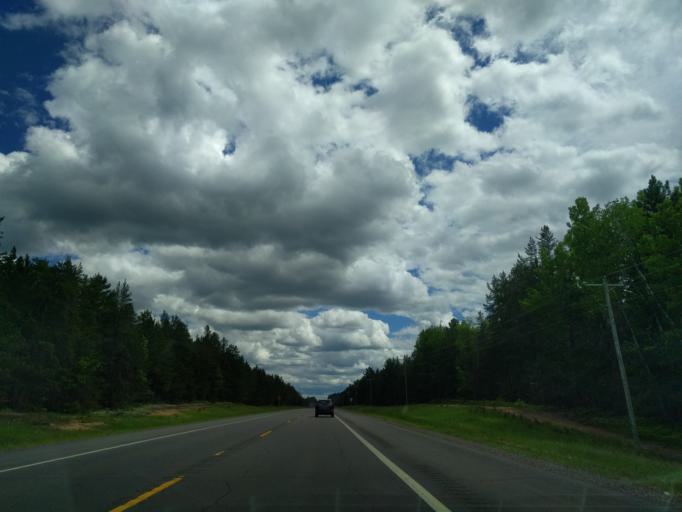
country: US
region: Michigan
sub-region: Marquette County
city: Harvey
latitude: 46.4468
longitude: -87.4228
